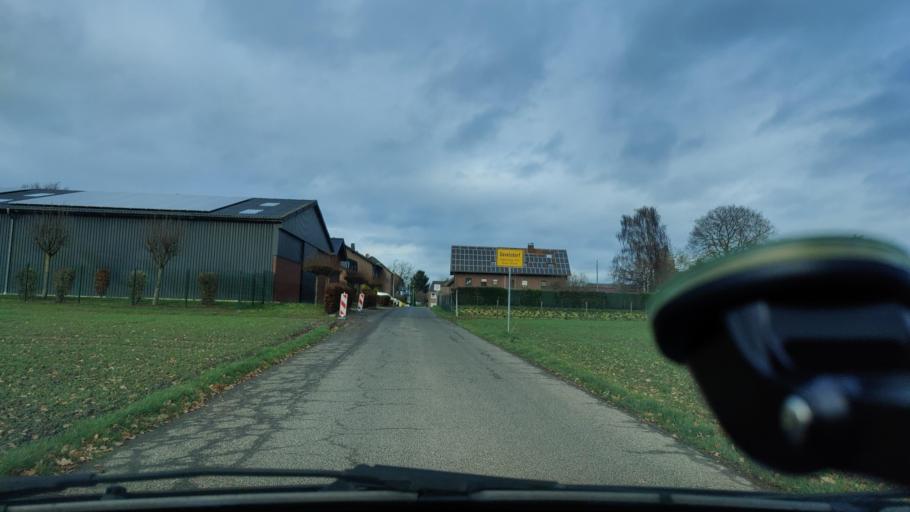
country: DE
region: North Rhine-Westphalia
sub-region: Regierungsbezirk Koln
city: Titz
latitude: 51.0066
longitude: 6.3867
